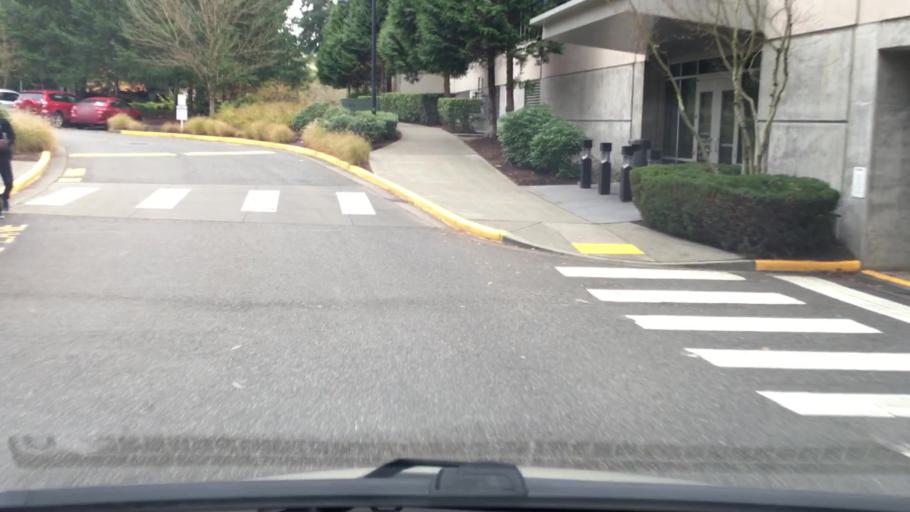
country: US
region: Washington
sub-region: King County
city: Redmond
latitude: 47.6432
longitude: -122.1256
